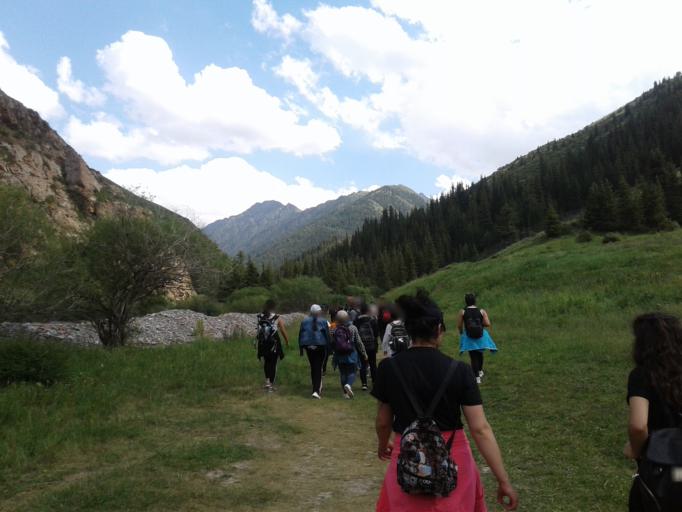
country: KG
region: Naryn
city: Naryn
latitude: 41.4575
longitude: 76.4527
